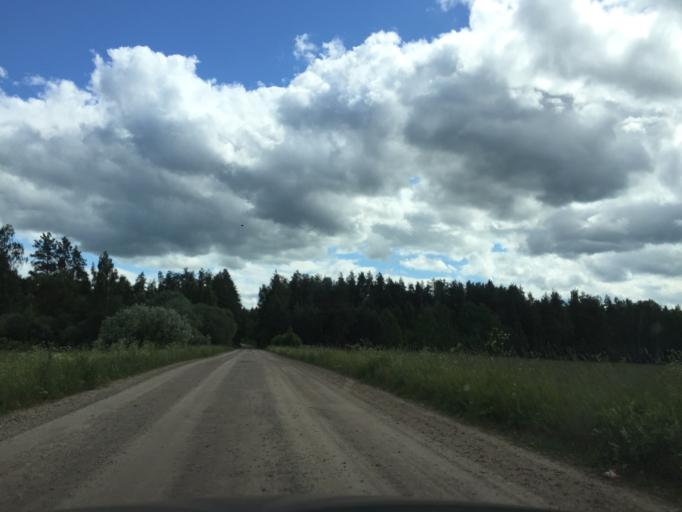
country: LV
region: Vecumnieki
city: Vecumnieki
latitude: 56.4971
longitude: 24.4076
